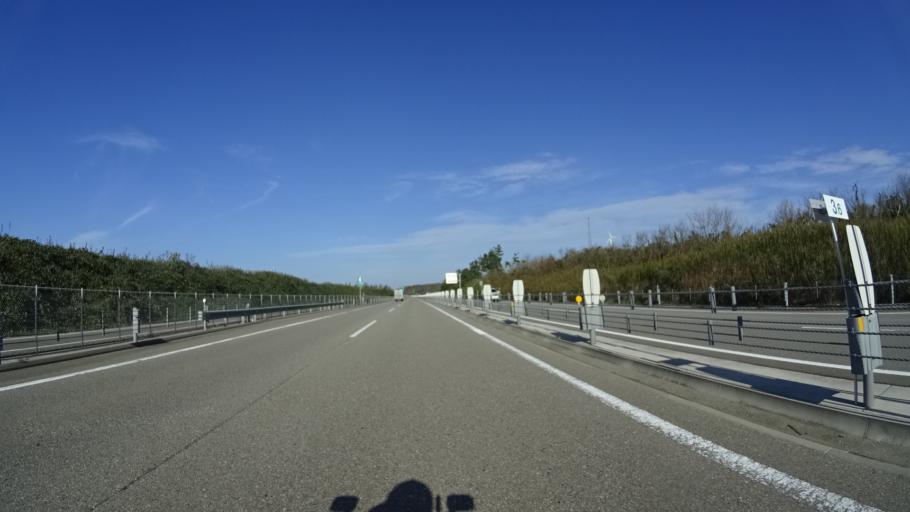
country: JP
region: Ishikawa
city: Kanazawa-shi
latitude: 36.6578
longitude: 136.6399
